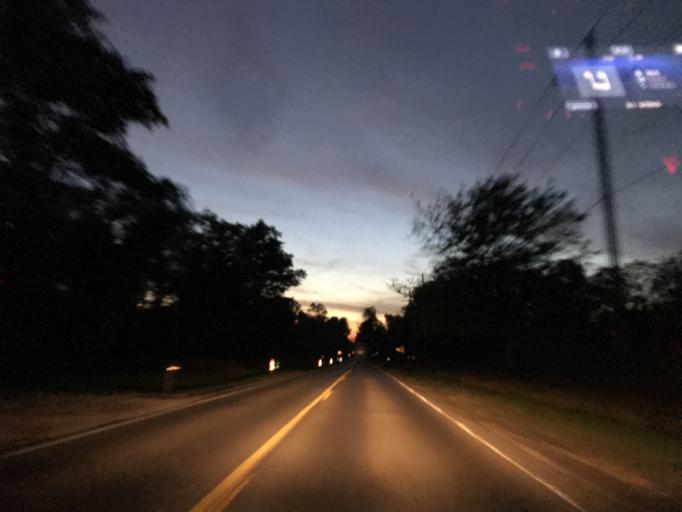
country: US
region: Michigan
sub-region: Oakland County
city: South Lyon
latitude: 42.4338
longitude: -83.5917
